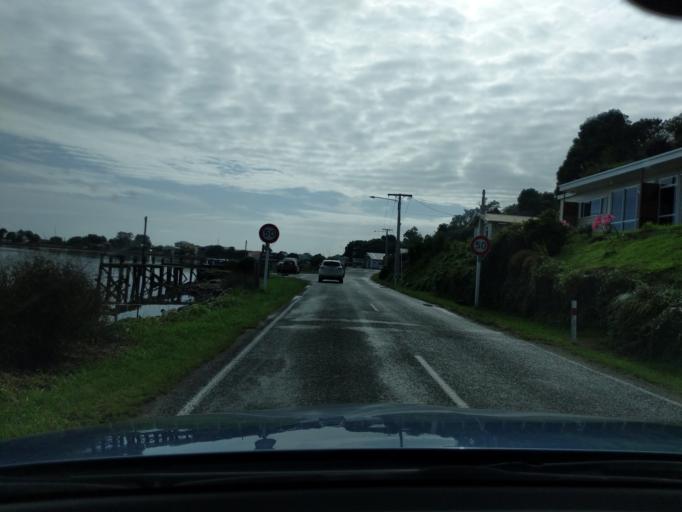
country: NZ
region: Tasman
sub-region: Tasman District
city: Takaka
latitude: -40.6794
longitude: 172.6786
